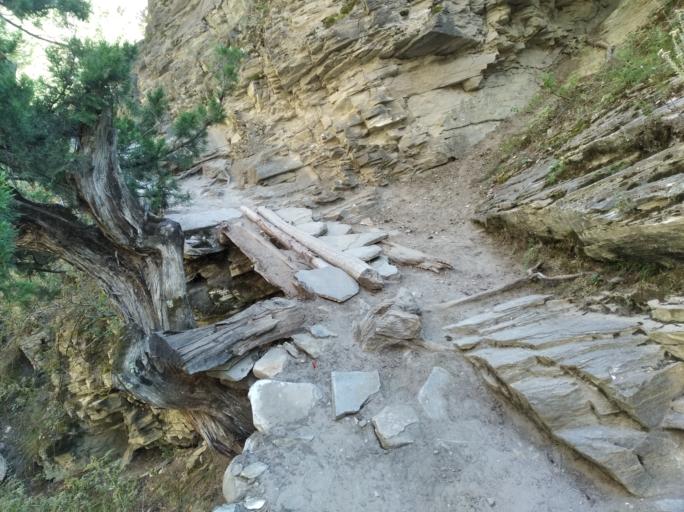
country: NP
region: Western Region
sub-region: Dhawalagiri Zone
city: Jomsom
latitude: 28.8781
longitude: 83.1259
